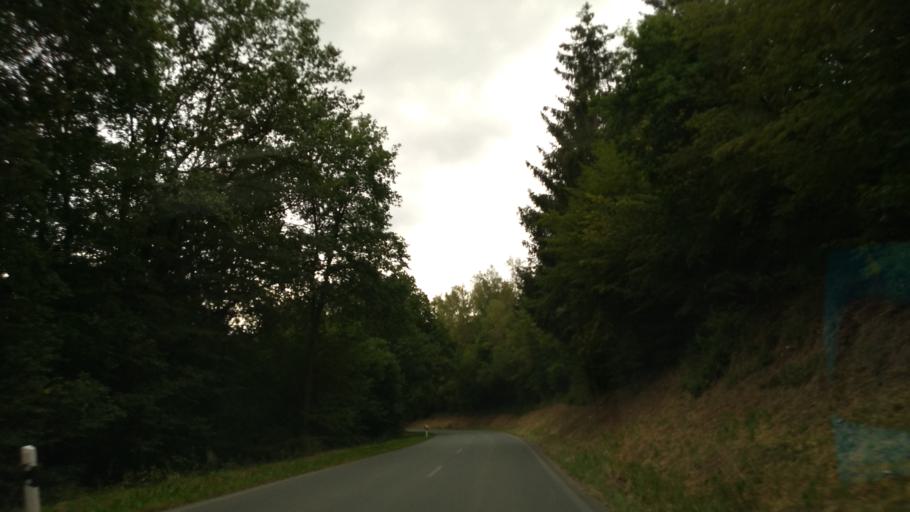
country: DE
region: North Rhine-Westphalia
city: Balve
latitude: 51.2916
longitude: 7.8853
